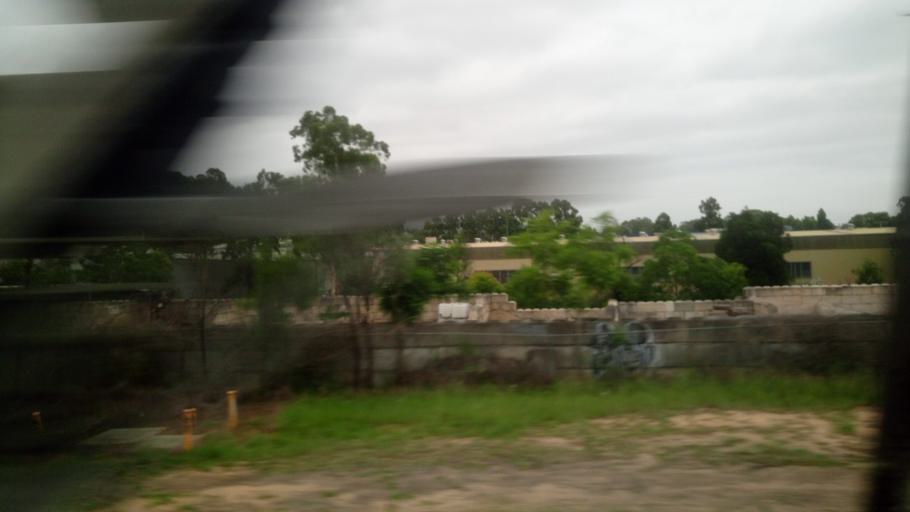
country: AU
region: New South Wales
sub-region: Penrith Municipality
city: Emu Heights
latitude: -33.7484
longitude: 150.6569
